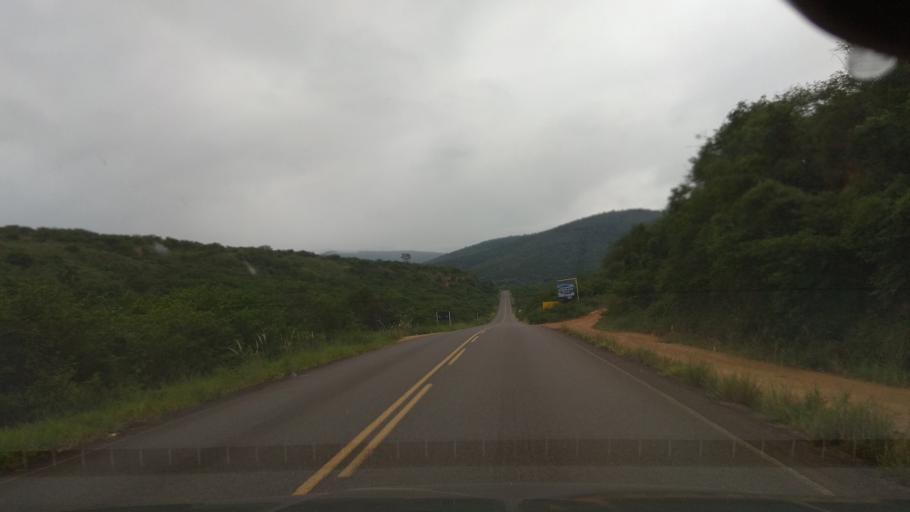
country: BR
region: Bahia
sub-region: Santa Ines
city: Santa Ines
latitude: -13.2522
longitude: -39.7779
